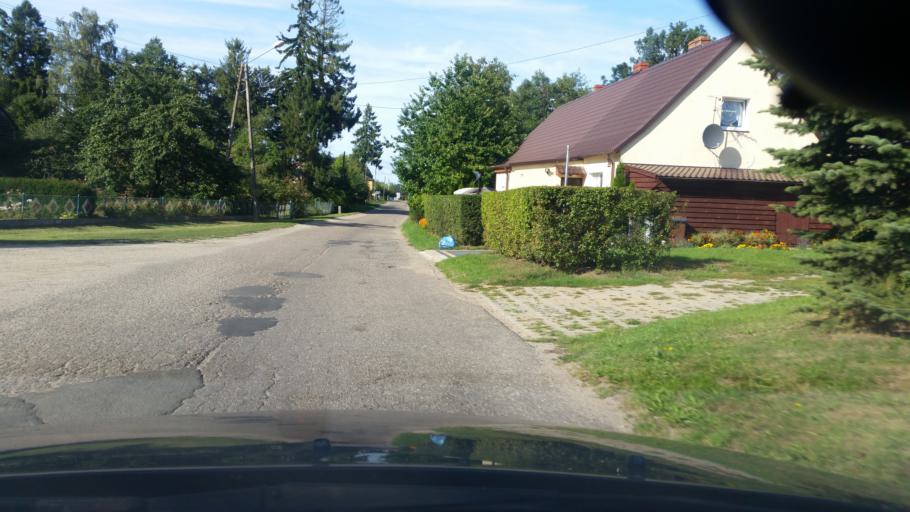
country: PL
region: Pomeranian Voivodeship
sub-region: Powiat wejherowski
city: Choczewo
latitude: 54.7675
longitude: 17.7935
